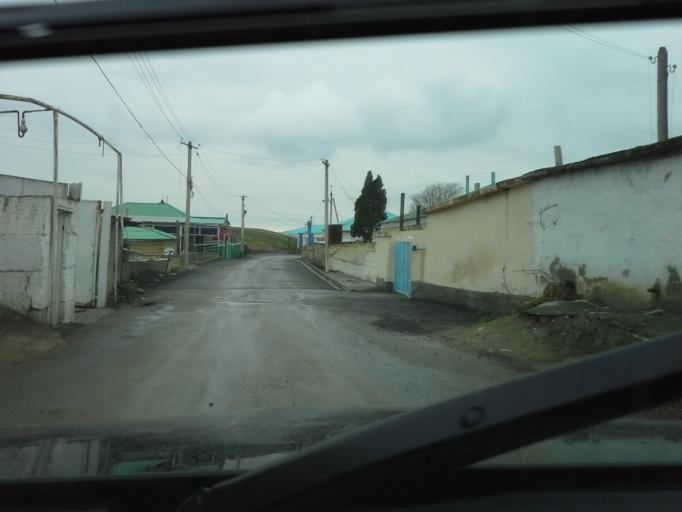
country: TM
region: Ahal
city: Abadan
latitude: 37.9588
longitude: 58.2074
